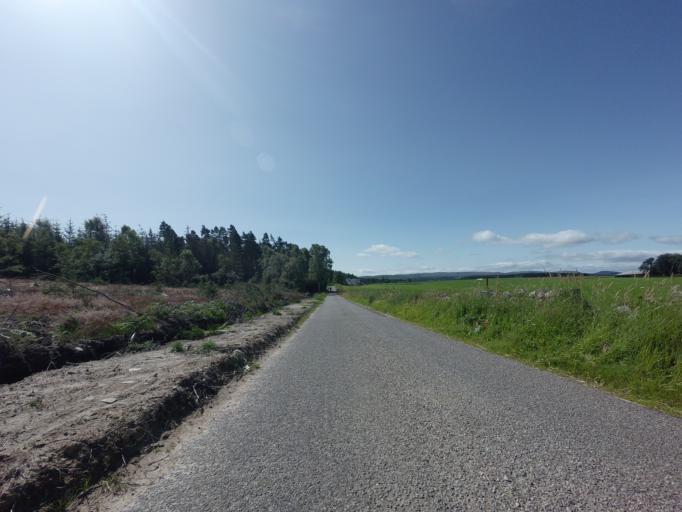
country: GB
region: Scotland
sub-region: Highland
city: Nairn
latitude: 57.5288
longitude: -3.8622
